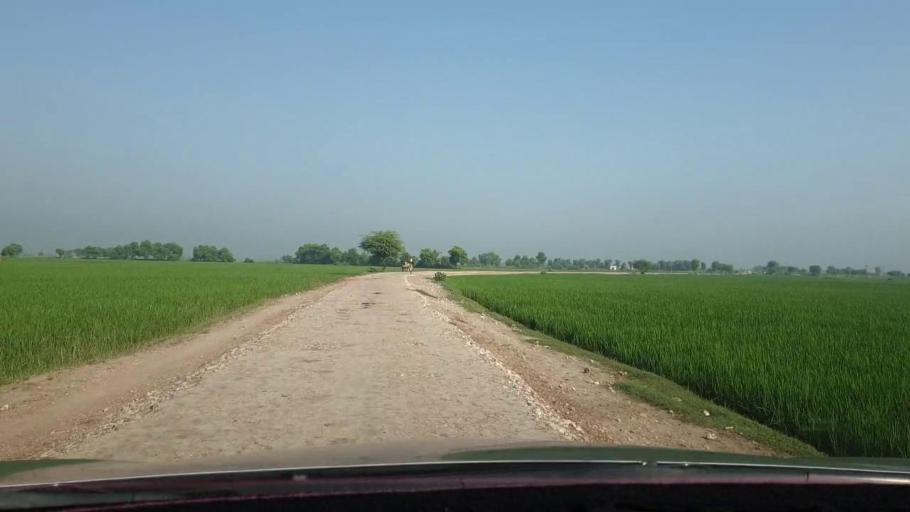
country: PK
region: Sindh
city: Nasirabad
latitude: 27.4293
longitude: 67.9210
